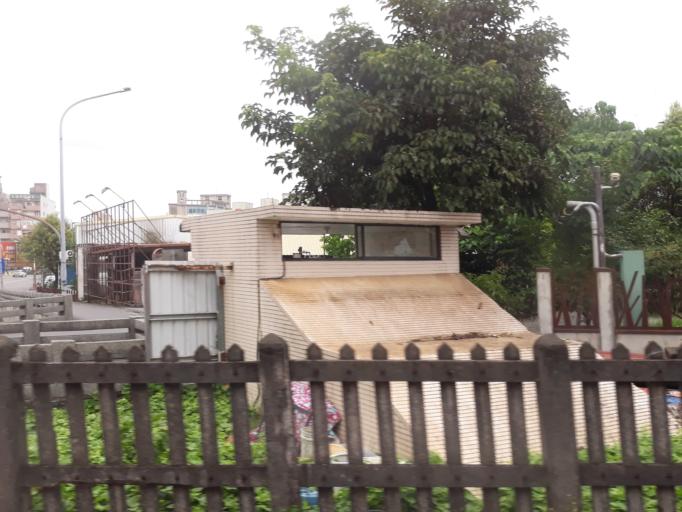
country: TW
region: Taiwan
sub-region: Yilan
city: Yilan
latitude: 24.6807
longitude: 121.7746
